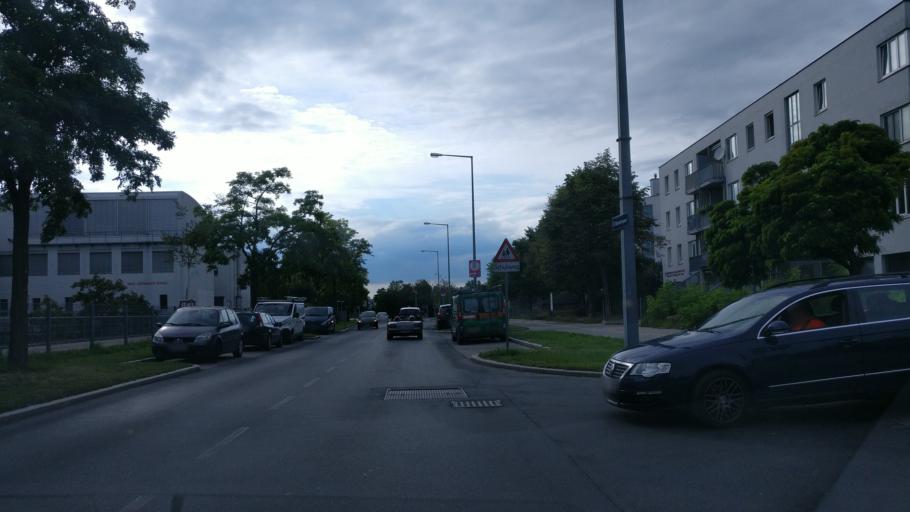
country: AT
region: Lower Austria
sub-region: Politischer Bezirk Korneuburg
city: Hagenbrunn
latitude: 48.2846
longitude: 16.4115
